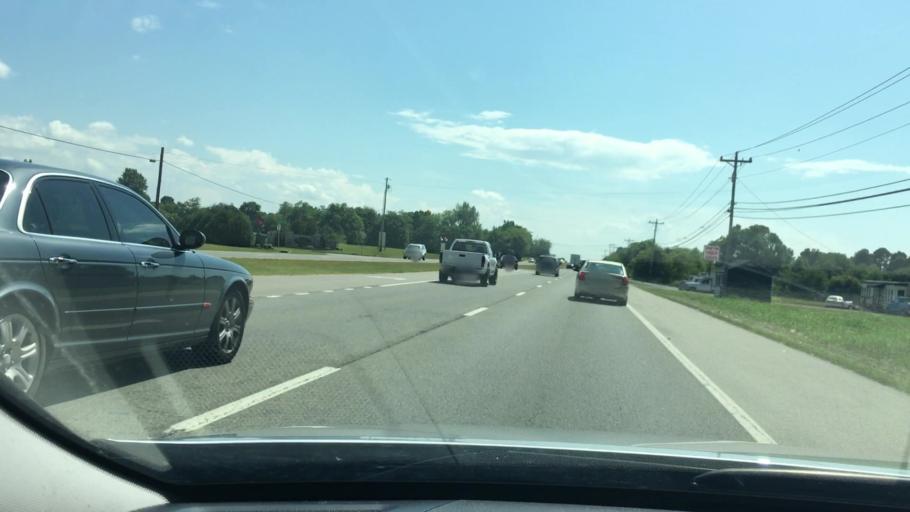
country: US
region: Tennessee
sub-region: Maury County
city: Spring Hill
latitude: 35.6935
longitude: -86.9891
